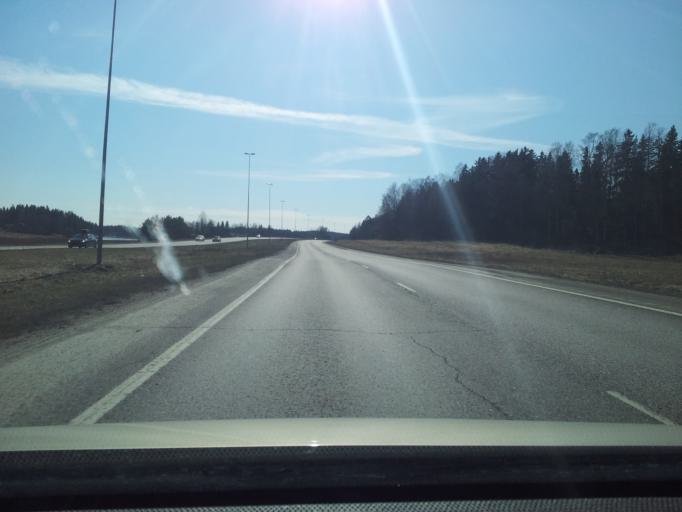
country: FI
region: Uusimaa
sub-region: Porvoo
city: Porvoo
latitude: 60.3647
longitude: 25.5508
